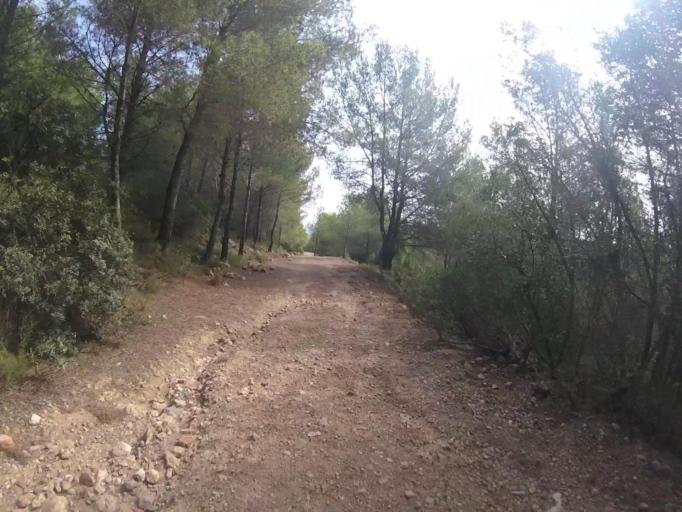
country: ES
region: Valencia
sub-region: Provincia de Castello
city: Benicassim
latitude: 40.0859
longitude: 0.0462
